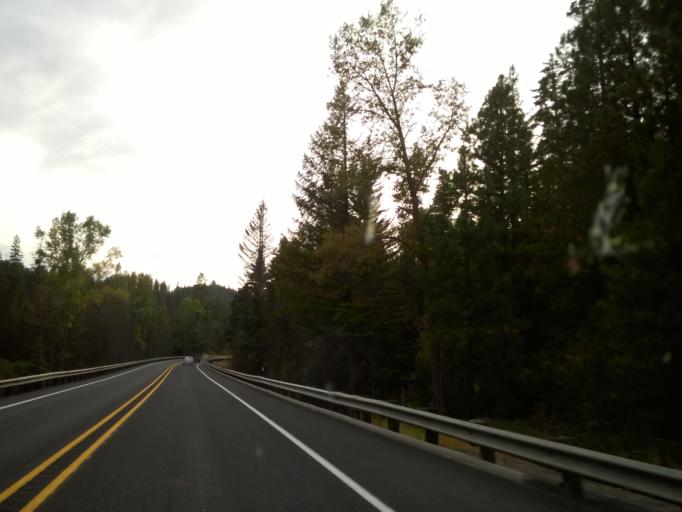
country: US
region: Washington
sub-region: Chelan County
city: Cashmere
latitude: 47.3317
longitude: -120.6425
